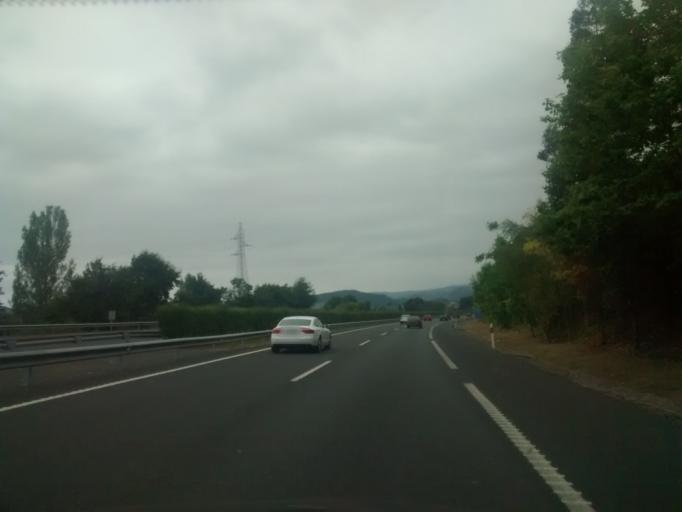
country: ES
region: Cantabria
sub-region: Provincia de Cantabria
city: Reocin
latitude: 43.3472
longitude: -4.1217
